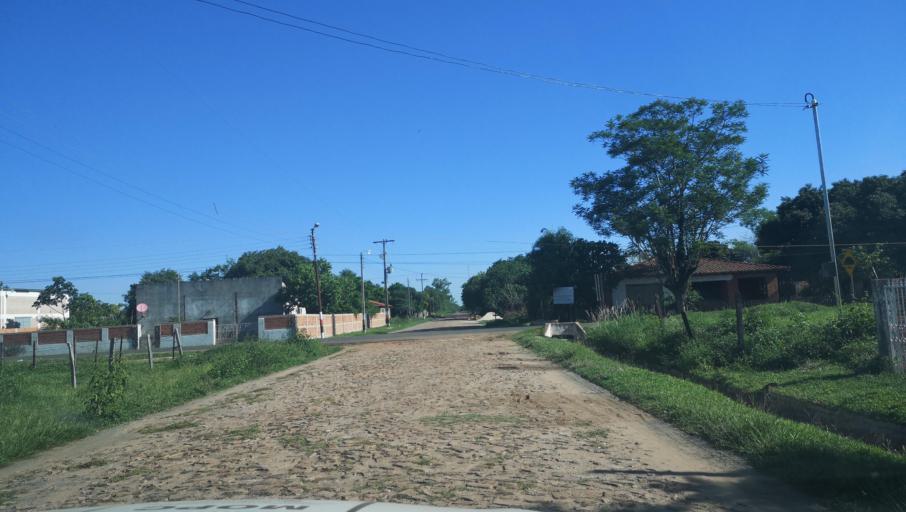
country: PY
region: Caaguazu
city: Carayao
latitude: -25.1961
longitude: -56.3985
